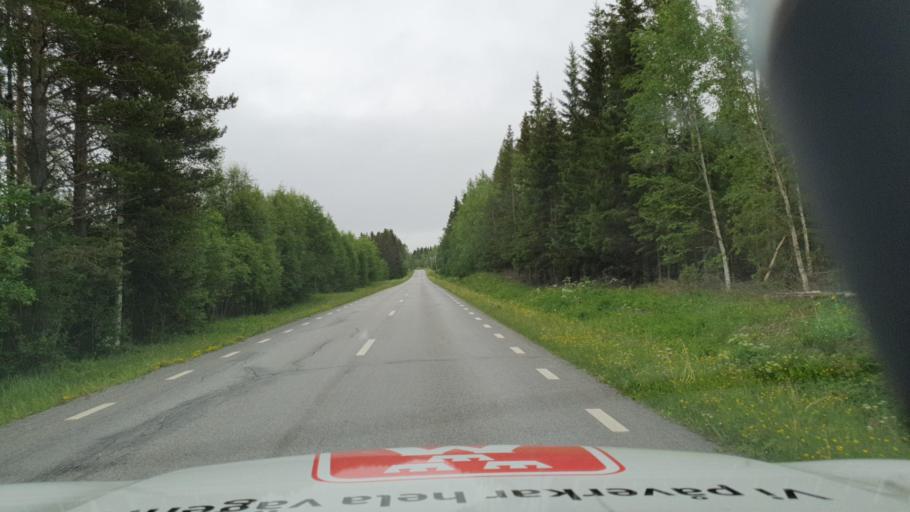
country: SE
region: Jaemtland
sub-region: Krokoms Kommun
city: Krokom
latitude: 63.1556
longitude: 14.1453
